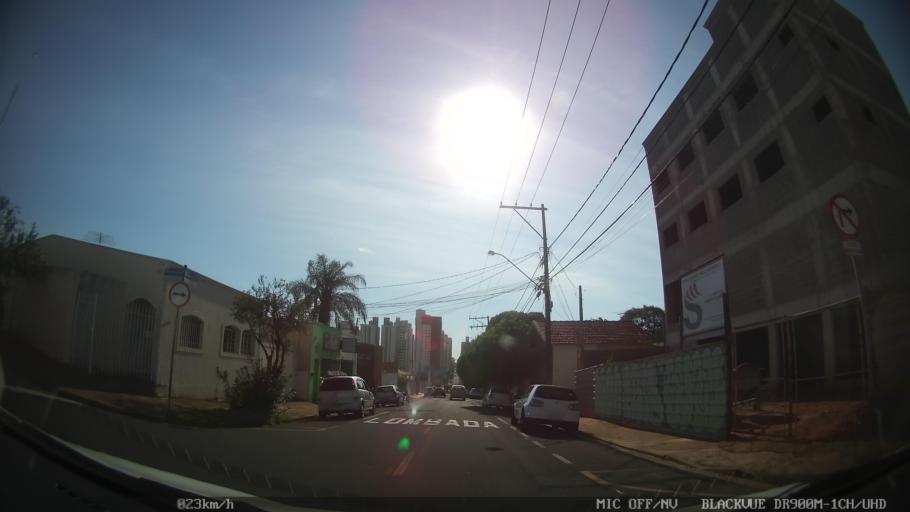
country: BR
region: Sao Paulo
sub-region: Sao Jose Do Rio Preto
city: Sao Jose do Rio Preto
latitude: -20.8190
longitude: -49.3795
